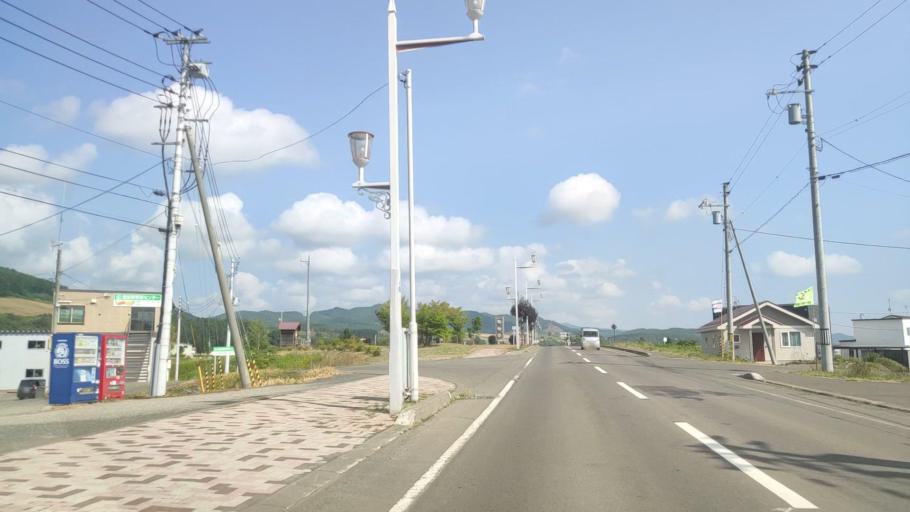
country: JP
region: Hokkaido
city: Shimo-furano
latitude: 43.3555
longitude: 142.3830
